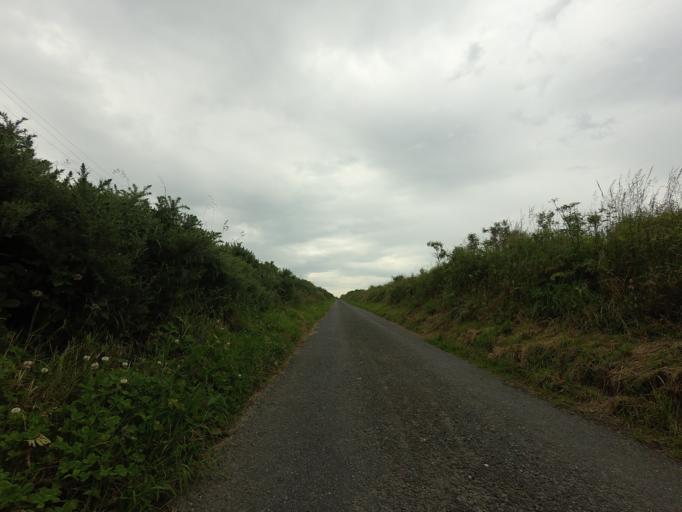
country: GB
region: Scotland
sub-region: Aberdeenshire
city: Whitehills
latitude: 57.6723
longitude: -2.5984
